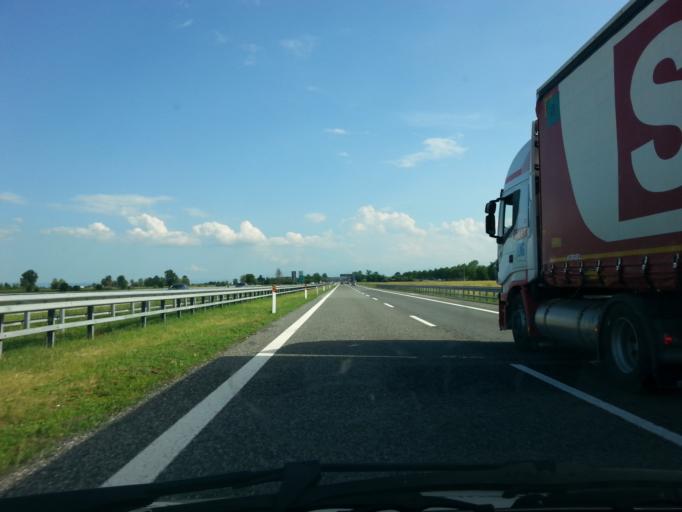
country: IT
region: Piedmont
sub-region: Provincia di Cuneo
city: Marene
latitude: 44.6857
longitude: 7.7685
